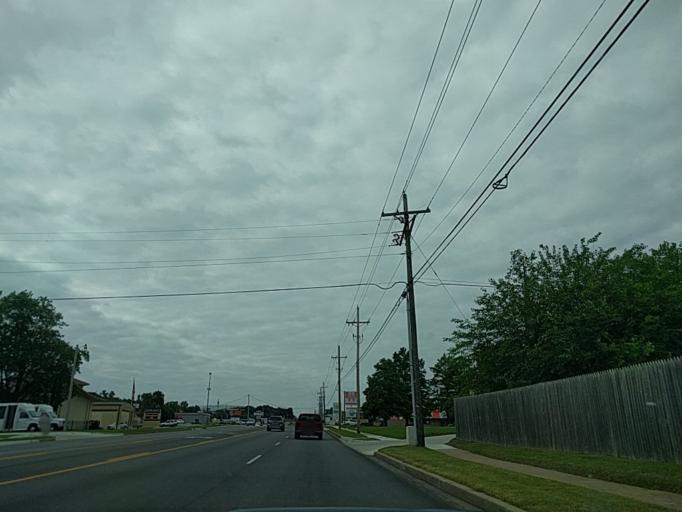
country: US
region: Oklahoma
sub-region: Tulsa County
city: Jenks
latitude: 36.0793
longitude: -95.9044
